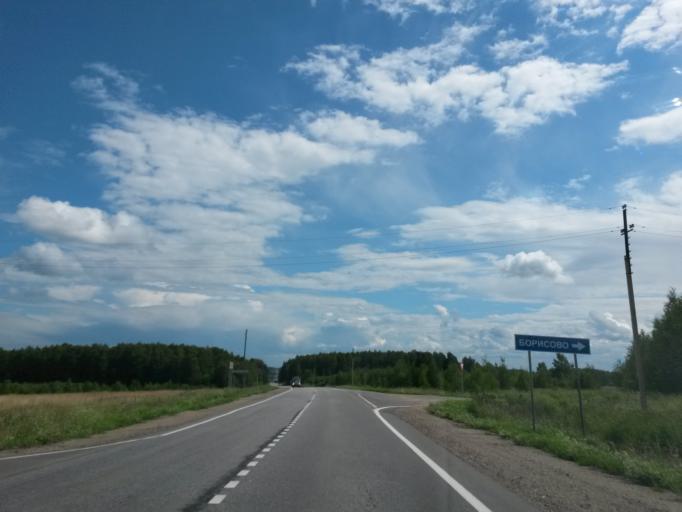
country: RU
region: Jaroslavl
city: Gavrilov-Yam
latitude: 57.2696
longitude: 39.9650
